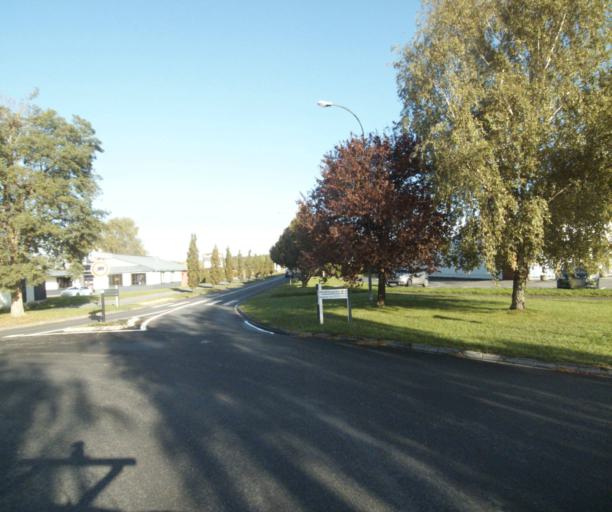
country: FR
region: Nord-Pas-de-Calais
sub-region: Departement du Nord
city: Lambersart
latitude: 50.6595
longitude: 3.0128
